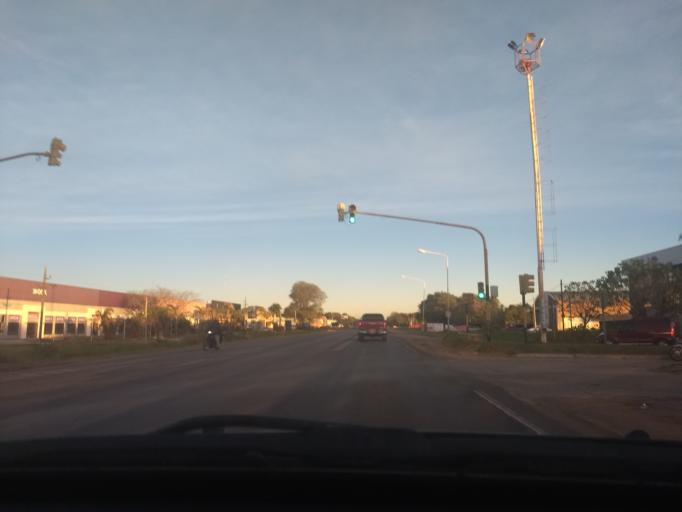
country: AR
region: Corrientes
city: Corrientes
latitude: -27.4902
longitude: -58.7798
